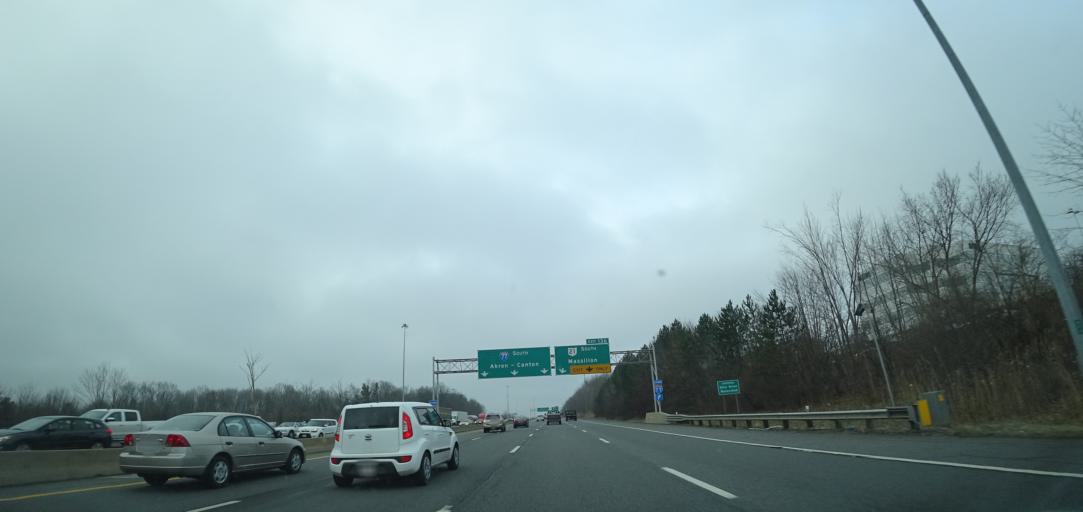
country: US
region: Ohio
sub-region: Summit County
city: Montrose-Ghent
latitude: 41.1300
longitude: -81.6521
